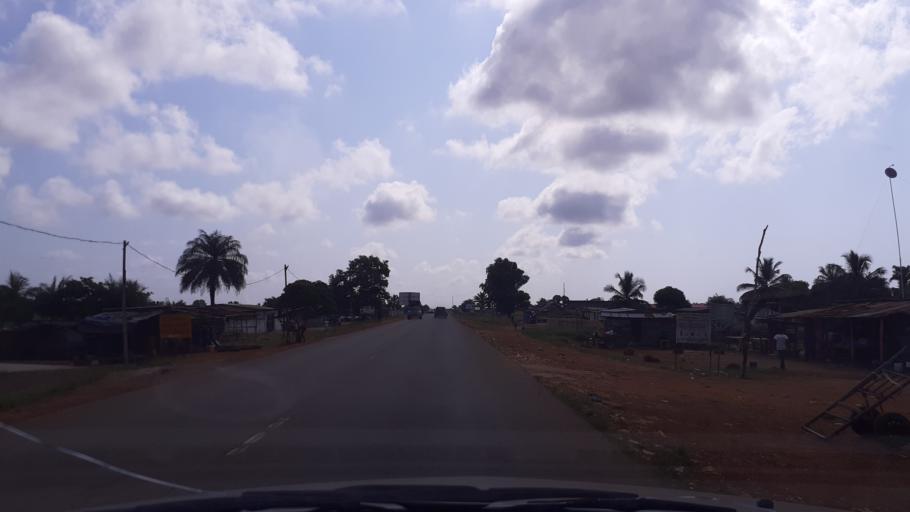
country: LR
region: Montserrado
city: Monrovia
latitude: 6.2225
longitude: -10.6017
